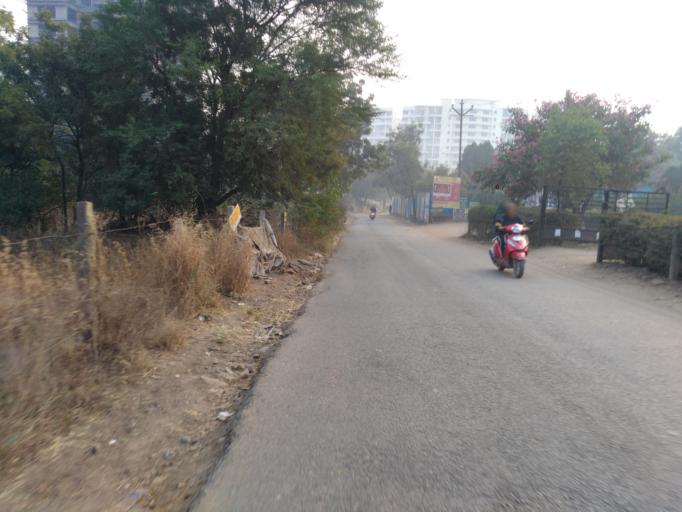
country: IN
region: Maharashtra
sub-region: Pune Division
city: Pune
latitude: 18.4601
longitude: 73.9000
